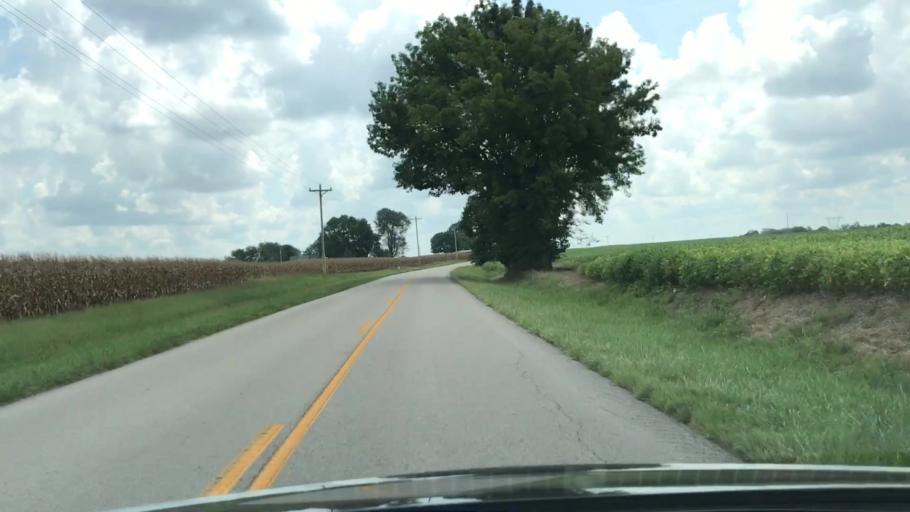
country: US
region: Kentucky
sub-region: Todd County
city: Elkton
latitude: 36.7812
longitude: -87.1230
